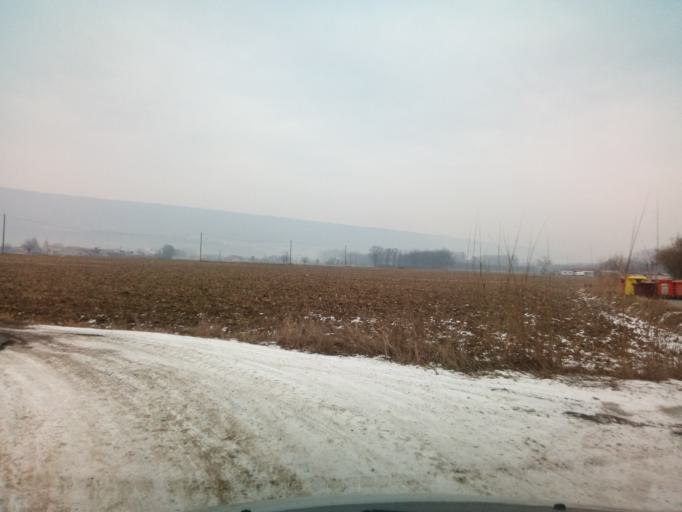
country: IT
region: Piedmont
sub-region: Provincia di Torino
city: Cascinette d'Ivrea
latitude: 45.4622
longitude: 7.9097
